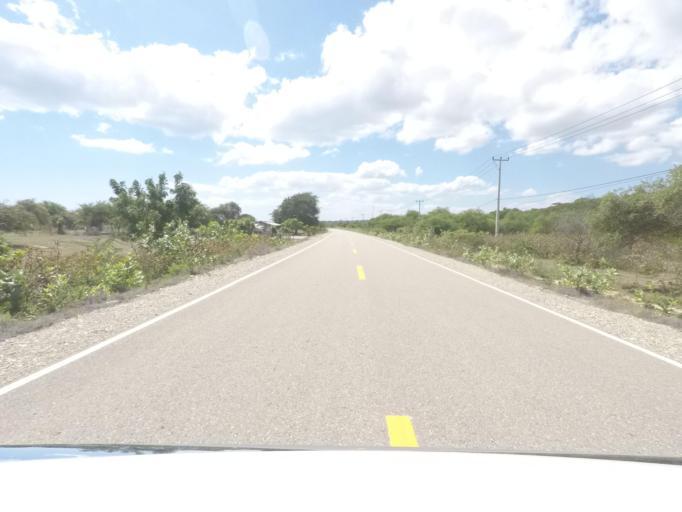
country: TL
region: Baucau
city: Baucau
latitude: -8.4229
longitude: 126.7026
